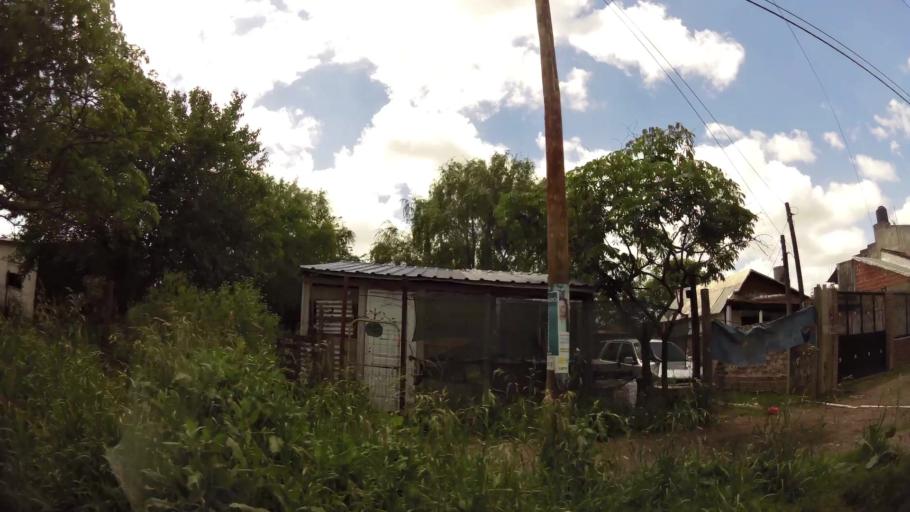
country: AR
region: Buenos Aires
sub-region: Partido de Quilmes
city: Quilmes
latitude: -34.8271
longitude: -58.2455
